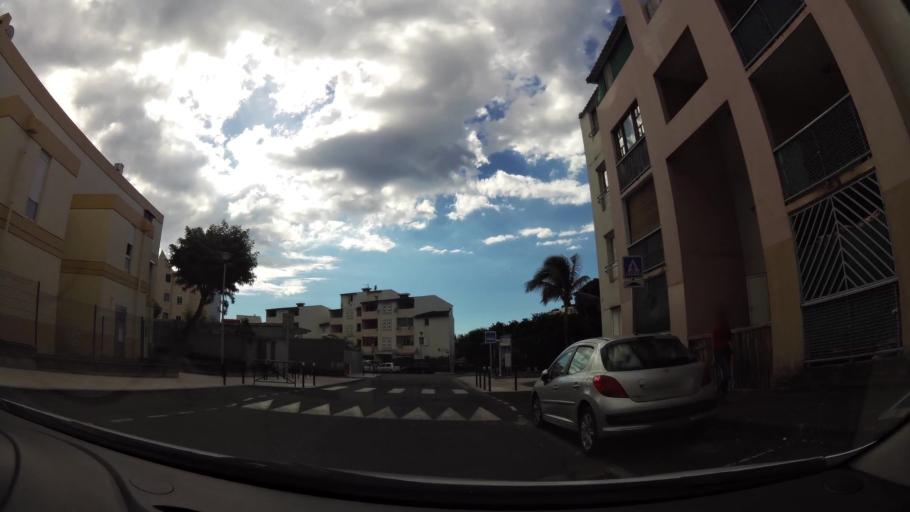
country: RE
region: Reunion
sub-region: Reunion
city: Saint-Denis
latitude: -20.8887
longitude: 55.4810
